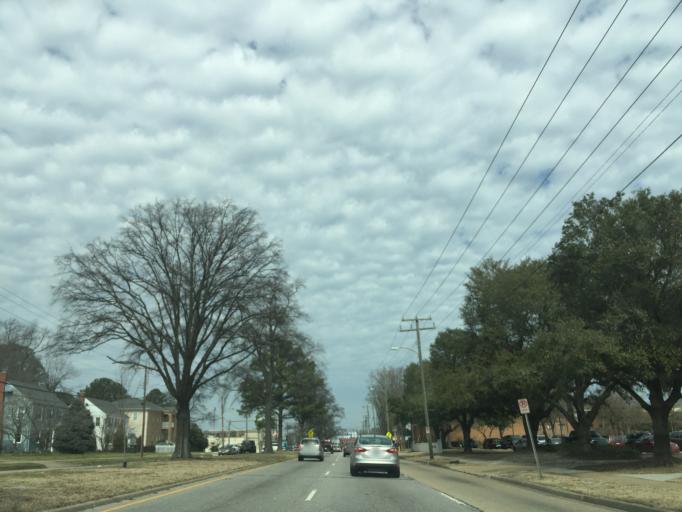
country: US
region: Virginia
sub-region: City of Norfolk
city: Norfolk
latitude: 36.9110
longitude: -76.2742
